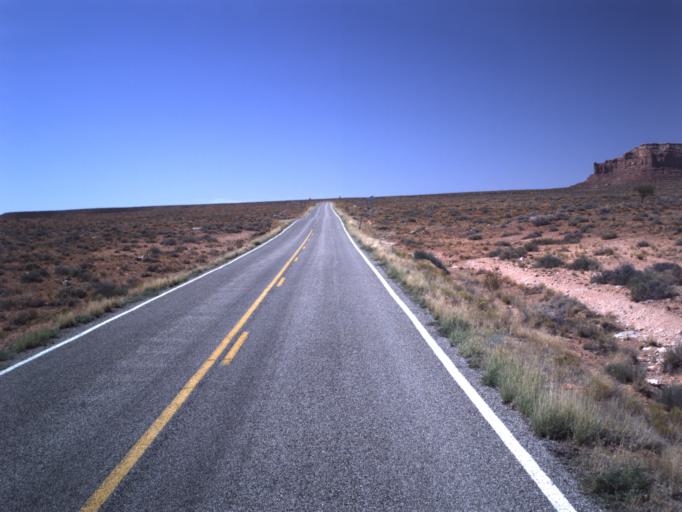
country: US
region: Utah
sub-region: San Juan County
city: Blanding
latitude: 37.2002
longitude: -109.8893
